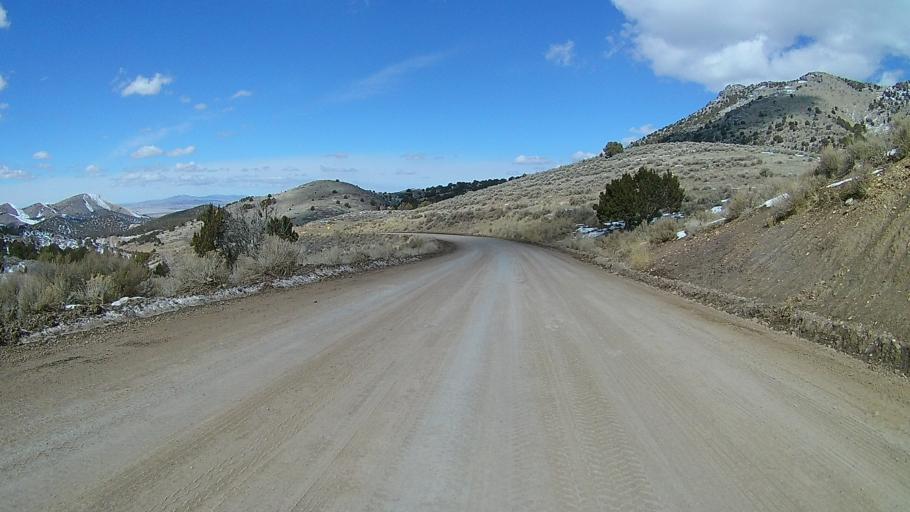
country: US
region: Utah
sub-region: Tooele County
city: Tooele
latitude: 40.1153
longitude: -112.5660
